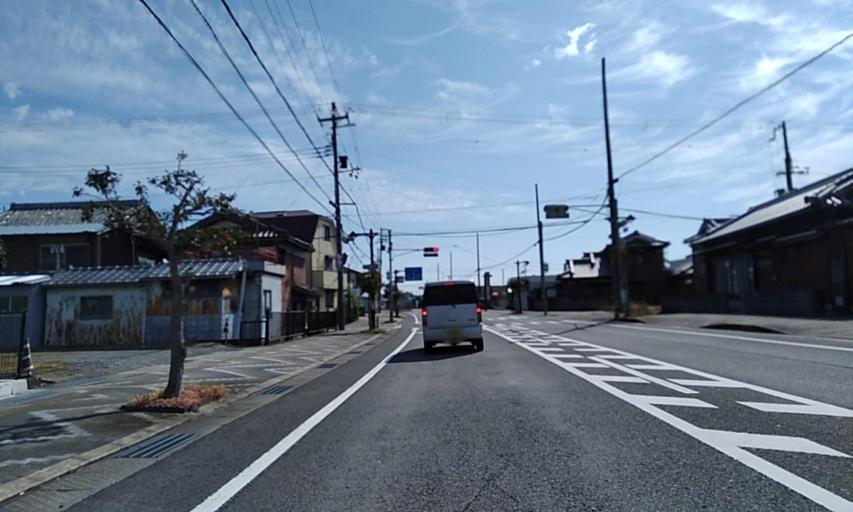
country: JP
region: Wakayama
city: Gobo
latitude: 33.9025
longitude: 135.1615
